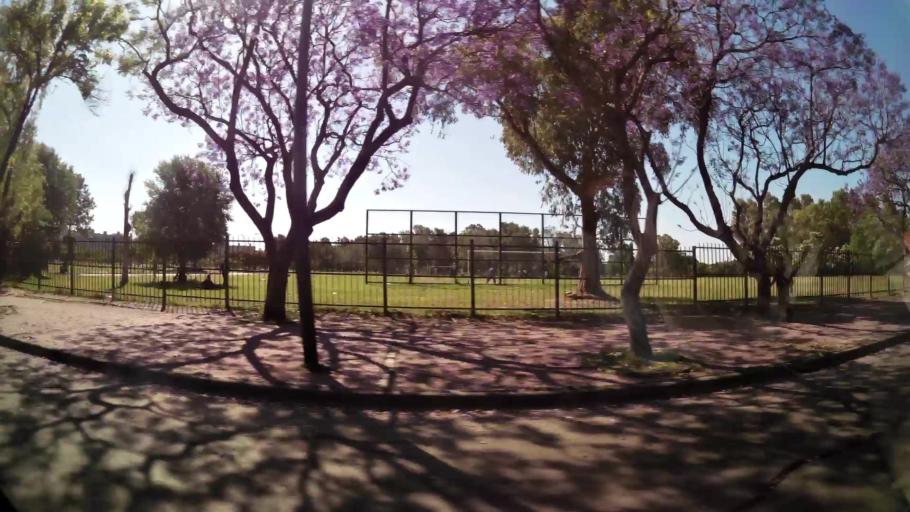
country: AR
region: Buenos Aires F.D.
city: Villa Lugano
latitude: -34.6843
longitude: -58.4553
